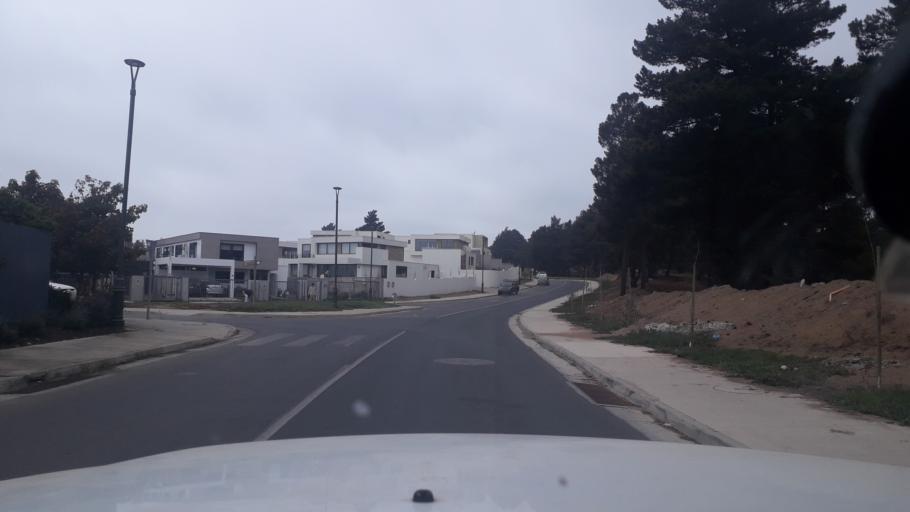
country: CL
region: Valparaiso
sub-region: Provincia de Valparaiso
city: Vina del Mar
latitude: -32.9474
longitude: -71.5377
